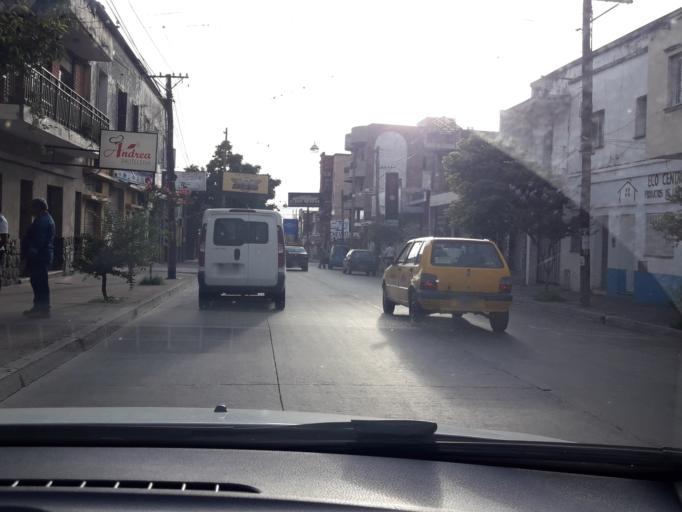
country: AR
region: Jujuy
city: San Salvador de Jujuy
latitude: -24.1913
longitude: -65.2997
